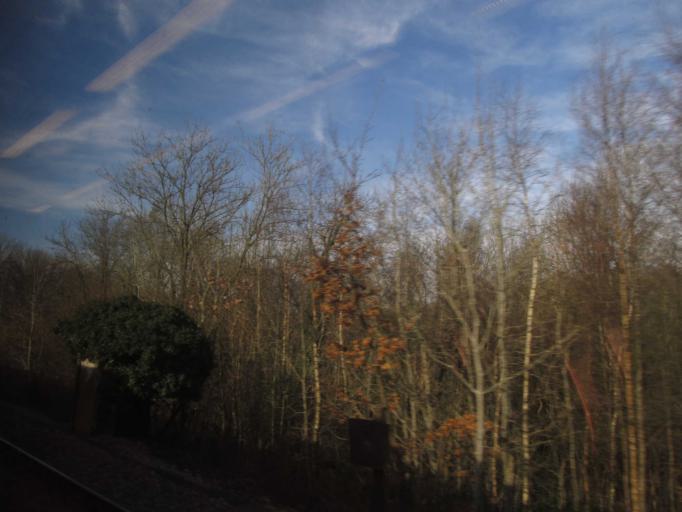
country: GB
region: England
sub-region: Surrey
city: Chiddingfold
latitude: 51.1266
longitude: -0.6595
